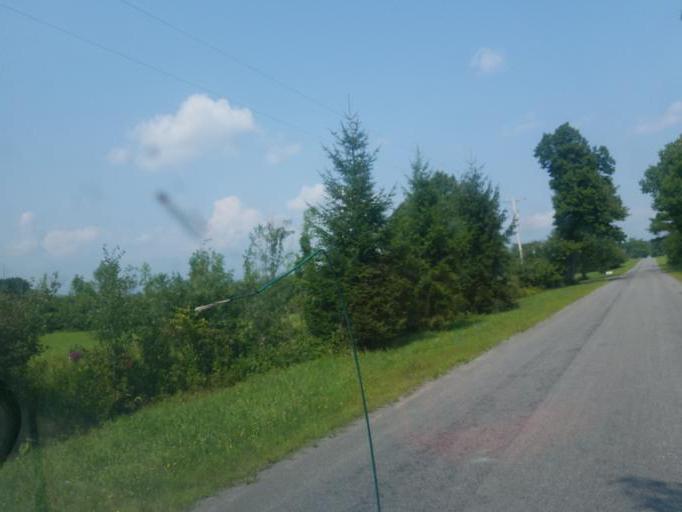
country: US
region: New York
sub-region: Montgomery County
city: Wellsville
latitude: 42.8534
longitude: -74.3413
